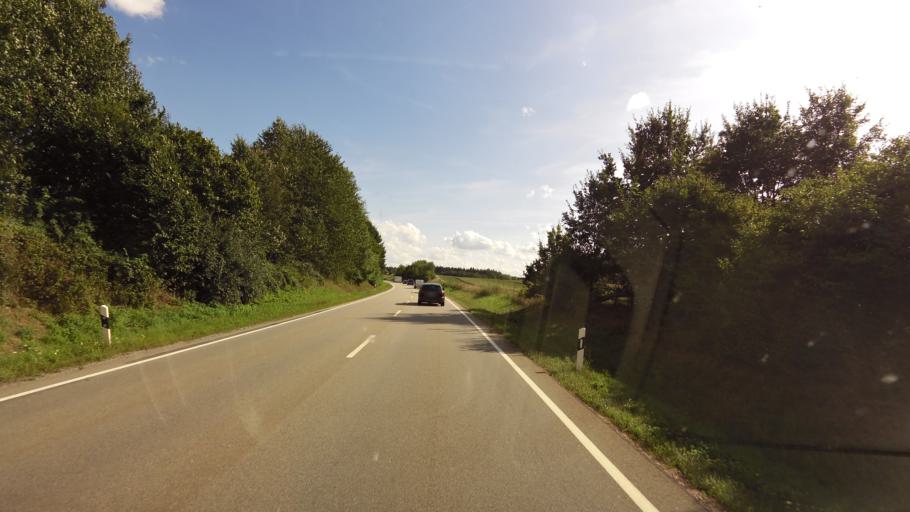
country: DE
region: Bavaria
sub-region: Lower Bavaria
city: Ascha
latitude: 48.9977
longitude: 12.6291
